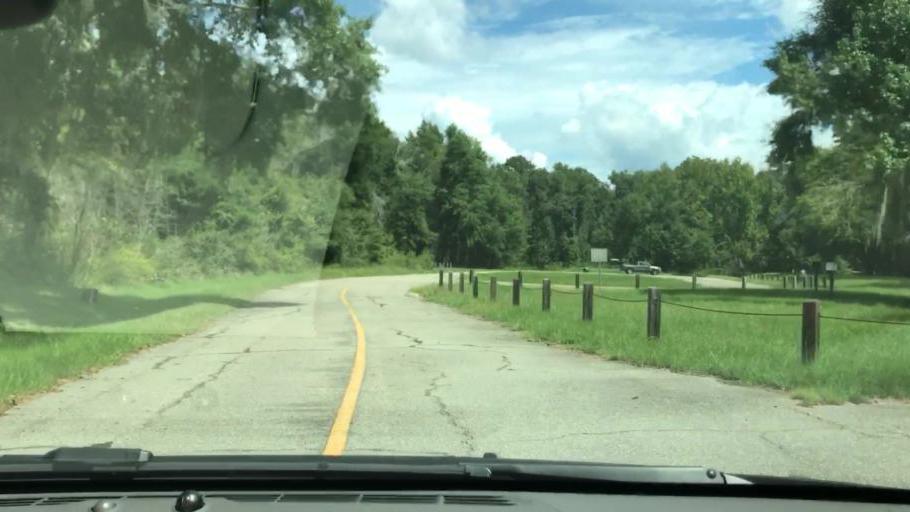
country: US
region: Georgia
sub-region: Quitman County
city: Georgetown
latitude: 32.0250
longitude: -85.0390
